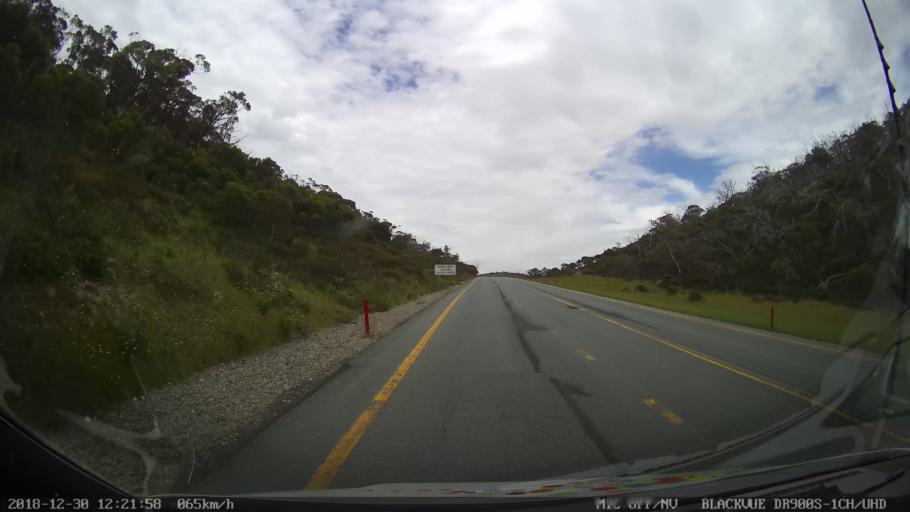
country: AU
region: New South Wales
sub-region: Snowy River
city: Jindabyne
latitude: -36.3559
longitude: 148.5142
